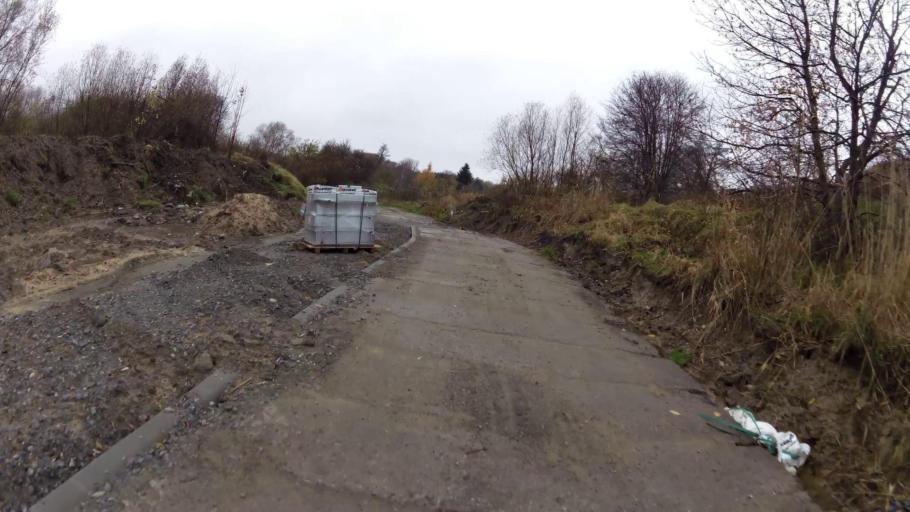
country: PL
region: West Pomeranian Voivodeship
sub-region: Koszalin
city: Koszalin
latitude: 54.2135
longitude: 16.1674
